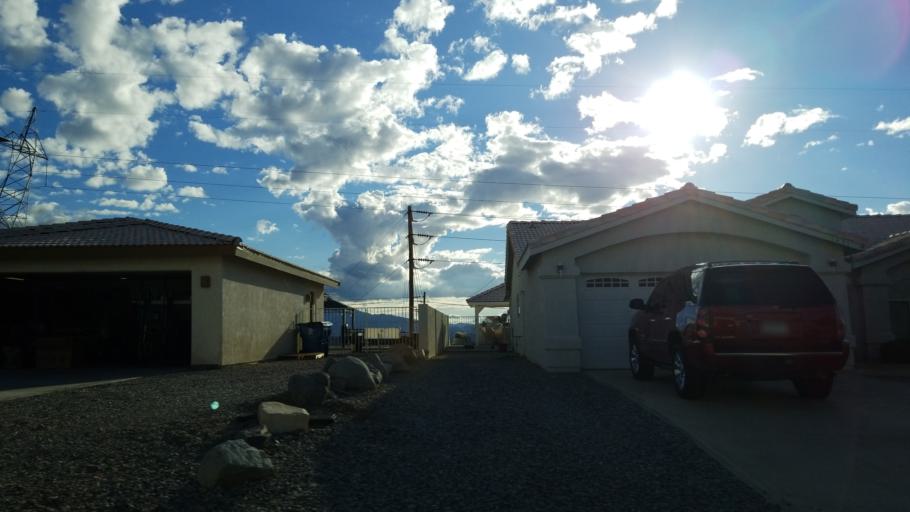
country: US
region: Arizona
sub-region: Mohave County
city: Lake Havasu City
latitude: 34.4661
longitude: -114.2585
